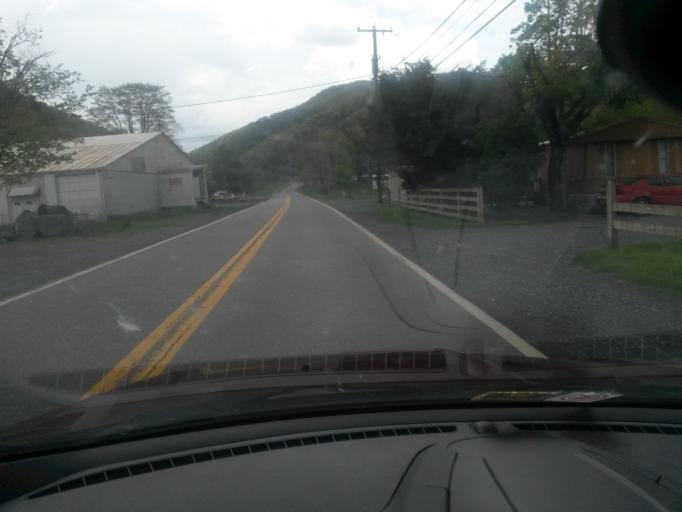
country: US
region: West Virginia
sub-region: Greenbrier County
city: White Sulphur Springs
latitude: 37.7934
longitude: -80.2740
